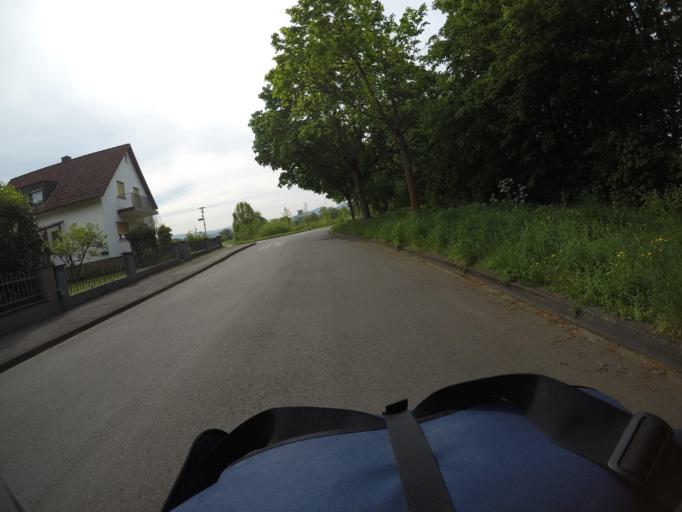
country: DE
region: Baden-Wuerttemberg
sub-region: Karlsruhe Region
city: Rastatt
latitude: 48.8510
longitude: 8.2207
